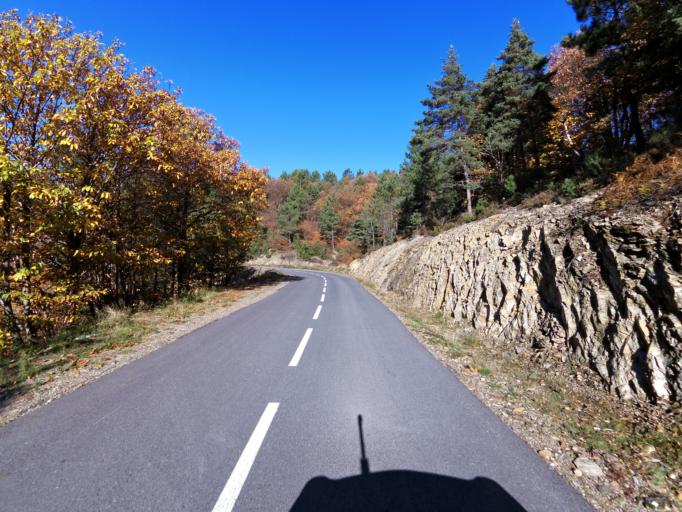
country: FR
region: Rhone-Alpes
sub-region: Departement de l'Ardeche
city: Les Vans
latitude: 44.5026
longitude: 4.1216
